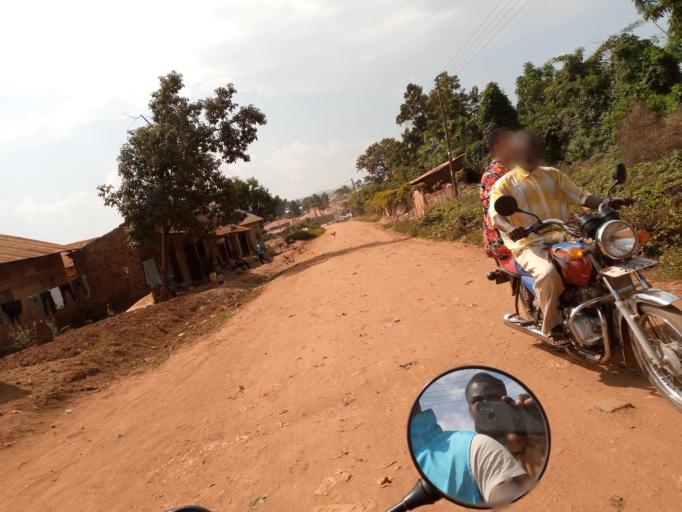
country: UG
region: Eastern Region
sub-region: Mbale District
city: Mbale
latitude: 1.0817
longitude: 34.1663
